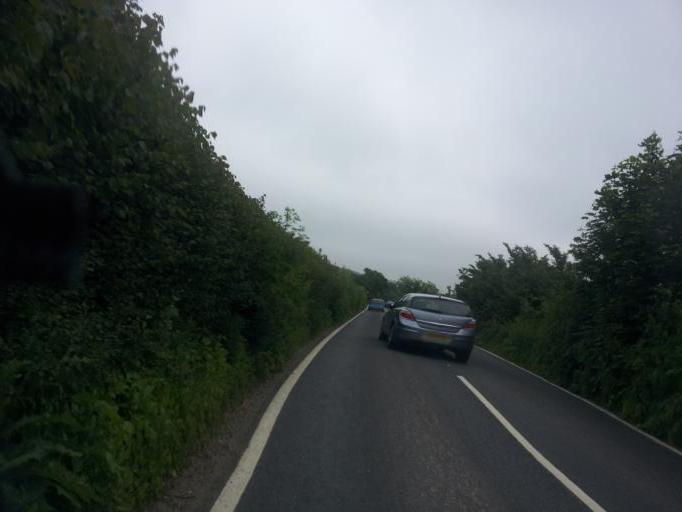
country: GB
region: England
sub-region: Kent
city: Boxley
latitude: 51.3080
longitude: 0.5390
